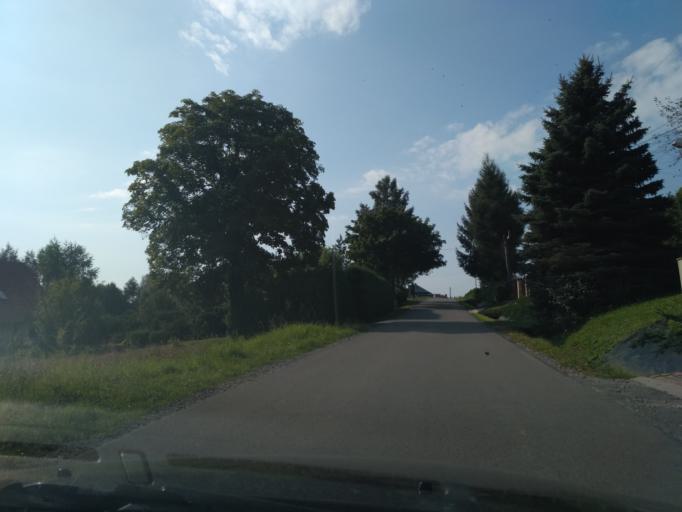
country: PL
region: Subcarpathian Voivodeship
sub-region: Powiat strzyzowski
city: Strzyzow
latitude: 49.8833
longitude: 21.7554
